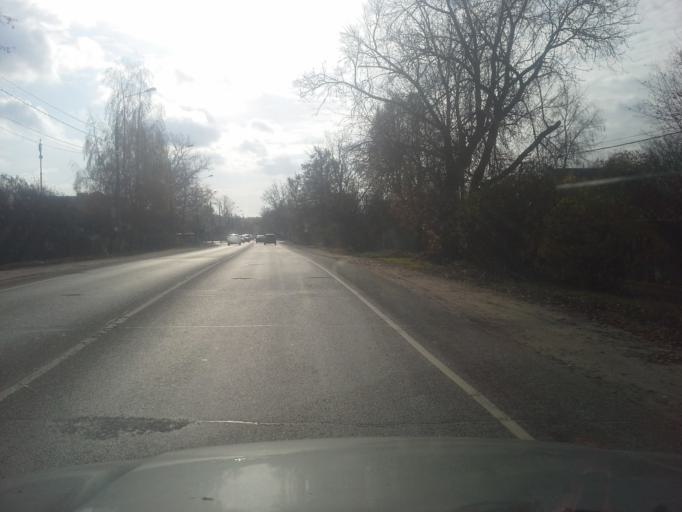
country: RU
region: Moskovskaya
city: Zvenigorod
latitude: 55.7235
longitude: 36.8630
